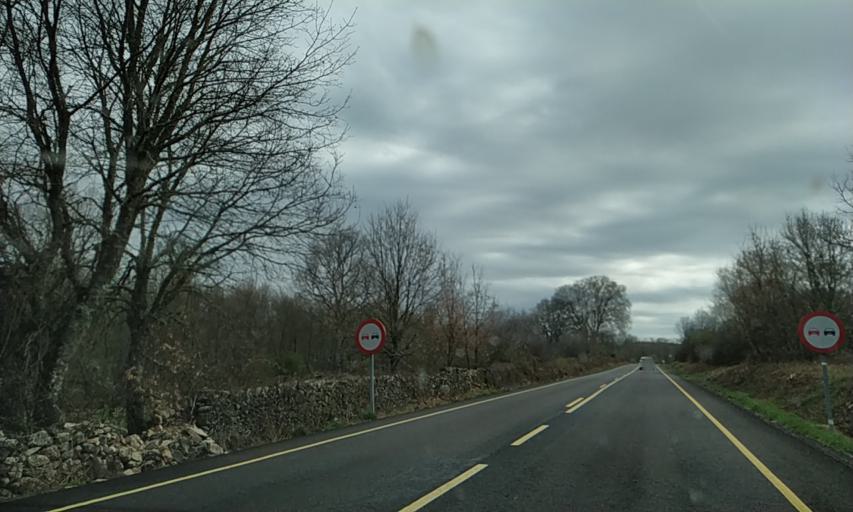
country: ES
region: Castille and Leon
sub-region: Provincia de Salamanca
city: Penaparda
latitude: 40.2768
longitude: -6.6789
